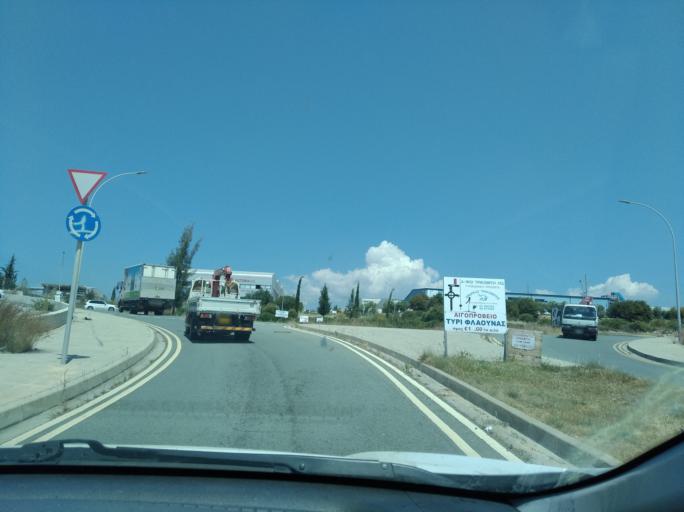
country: CY
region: Limassol
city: Ypsonas
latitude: 34.7248
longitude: 32.9473
